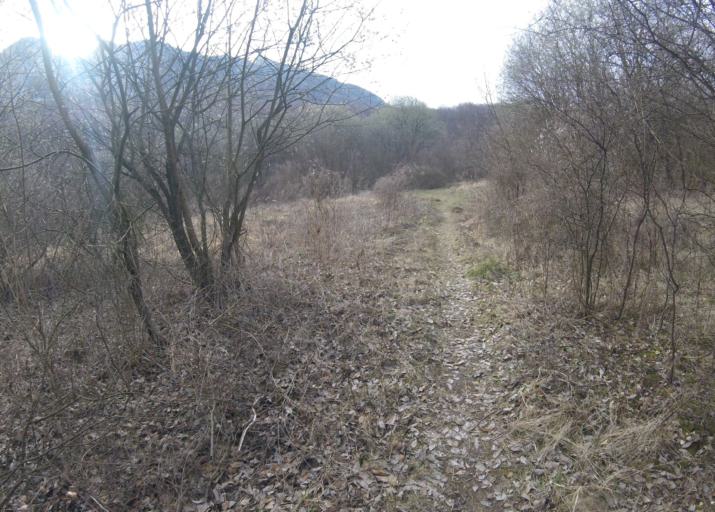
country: HU
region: Heves
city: Belapatfalva
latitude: 48.0481
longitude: 20.3666
